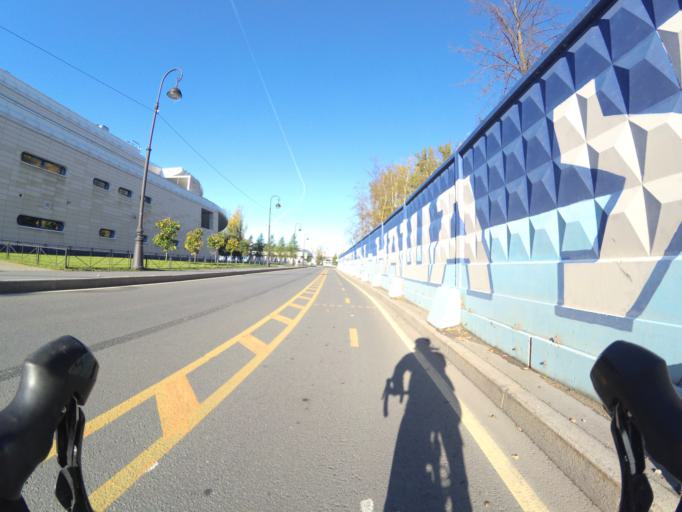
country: RU
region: St.-Petersburg
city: Staraya Derevnya
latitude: 59.9712
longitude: 30.2313
